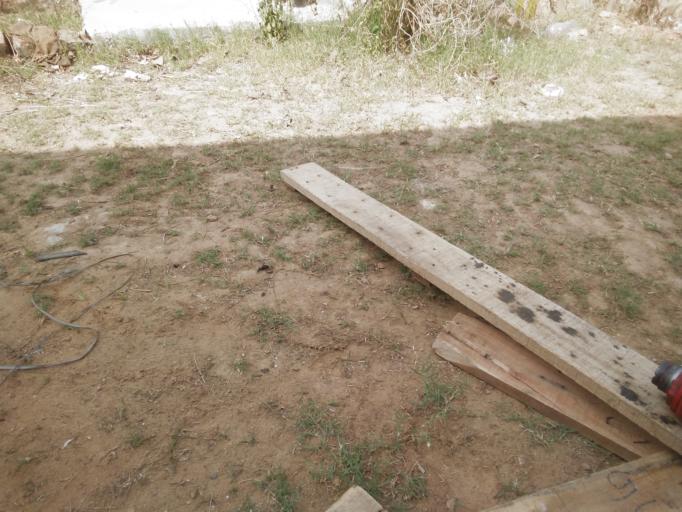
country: IN
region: Tripura
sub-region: West Tripura
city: Agartala
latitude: 23.8700
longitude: 91.2993
